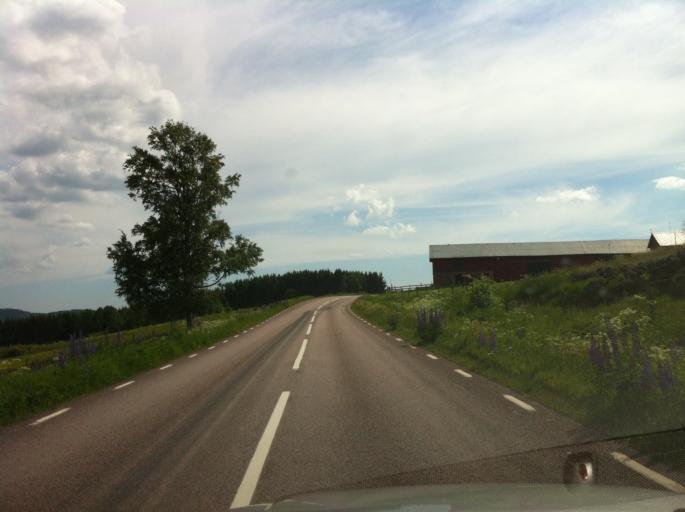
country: SE
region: Vaermland
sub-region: Sunne Kommun
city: Sunne
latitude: 59.7948
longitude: 13.1931
